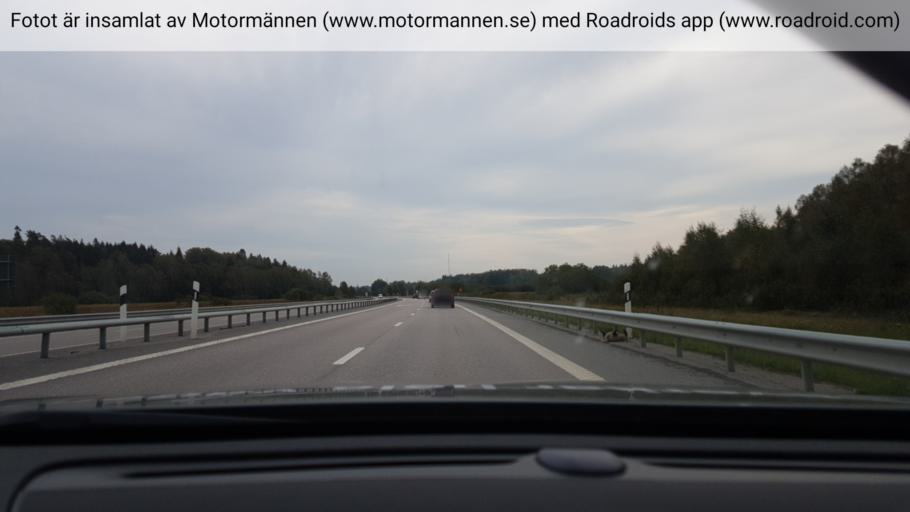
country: SE
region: Stockholm
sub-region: Nynashamns Kommun
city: Nynashamn
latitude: 58.9385
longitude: 17.9192
